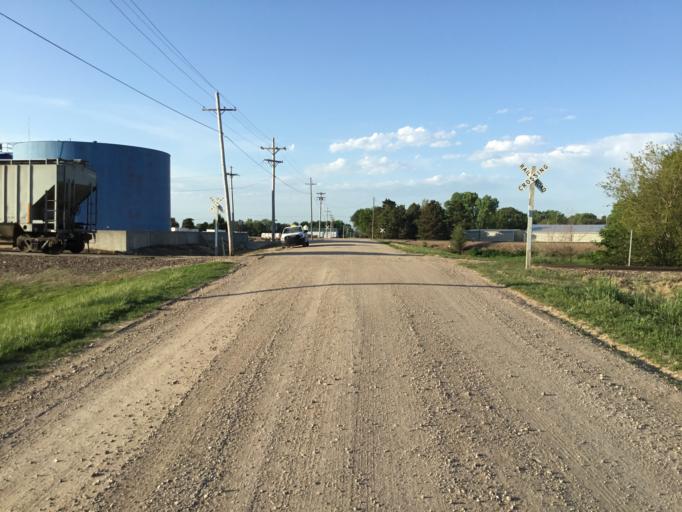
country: US
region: Kansas
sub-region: Mitchell County
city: Beloit
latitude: 39.4548
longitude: -98.0976
